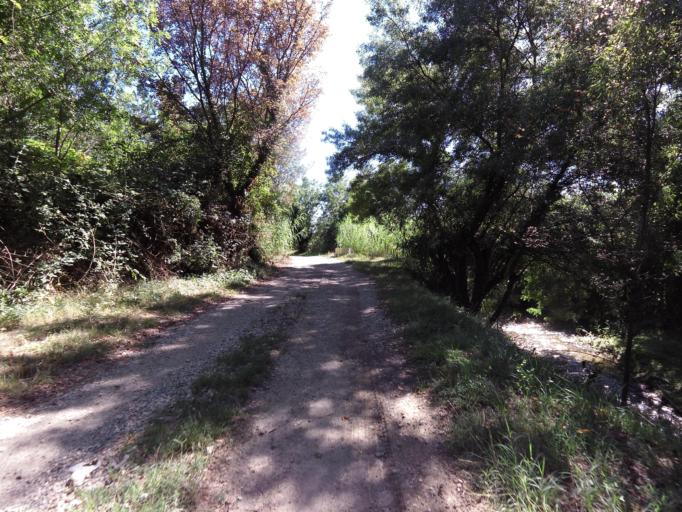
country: FR
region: Languedoc-Roussillon
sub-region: Departement du Gard
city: Vergeze
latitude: 43.7415
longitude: 4.2129
